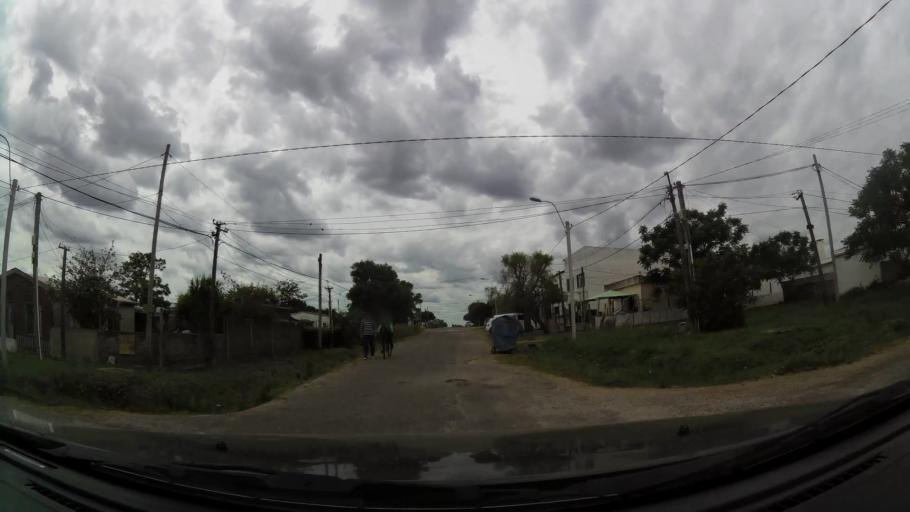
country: UY
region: Canelones
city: Las Piedras
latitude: -34.7183
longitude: -56.2099
